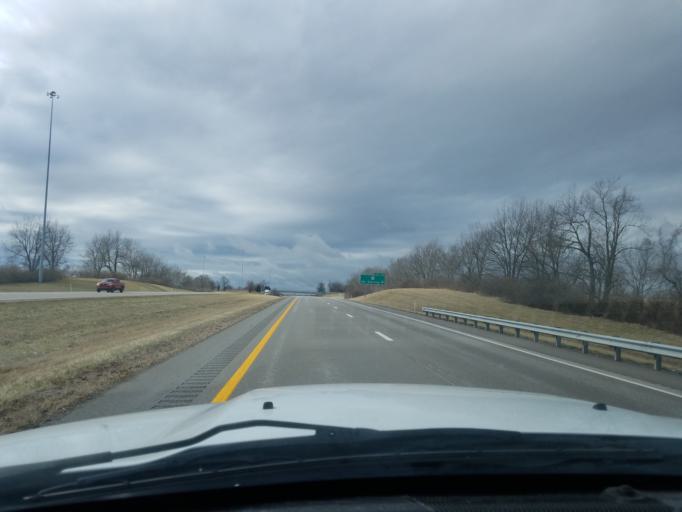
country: US
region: Kentucky
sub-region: Montgomery County
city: Mount Sterling
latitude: 38.0894
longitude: -83.8919
